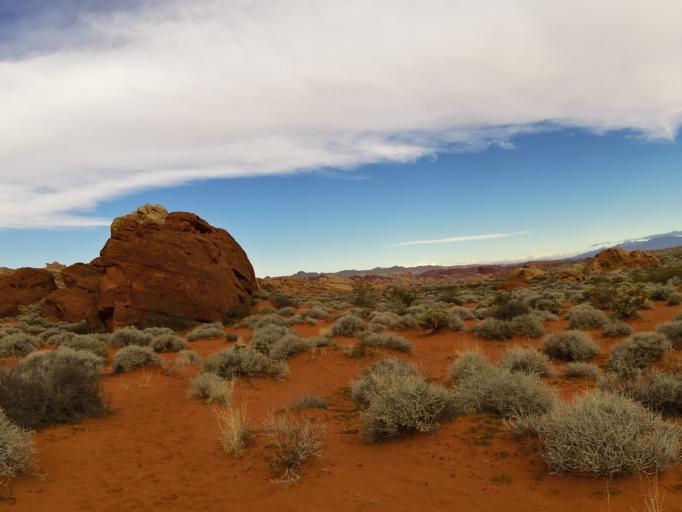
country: US
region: Nevada
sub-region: Clark County
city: Moapa Valley
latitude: 36.4502
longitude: -114.5133
